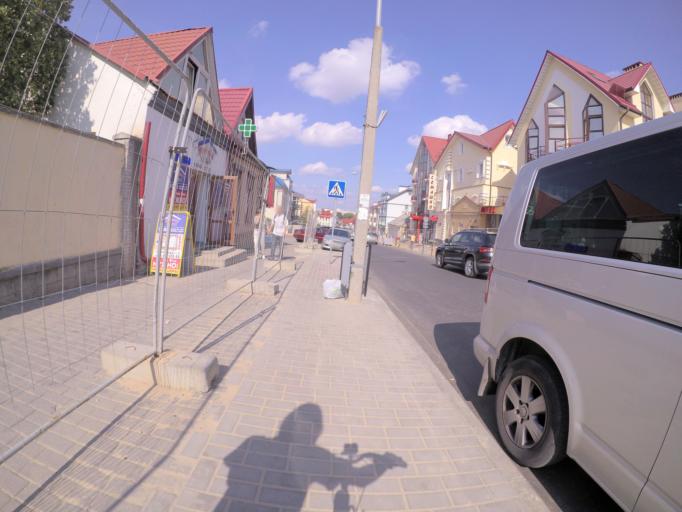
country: BY
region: Grodnenskaya
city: Hrodna
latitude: 53.6753
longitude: 23.8414
